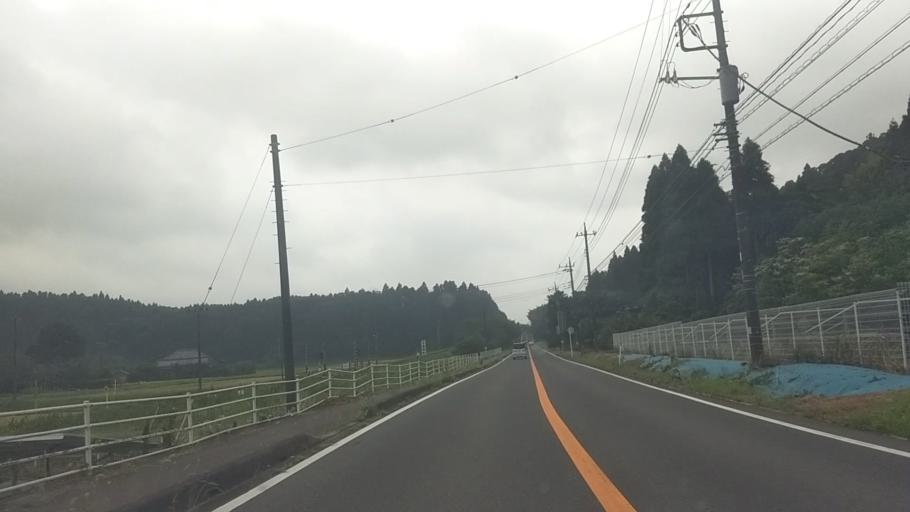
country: JP
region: Chiba
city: Ohara
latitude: 35.2716
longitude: 140.3323
